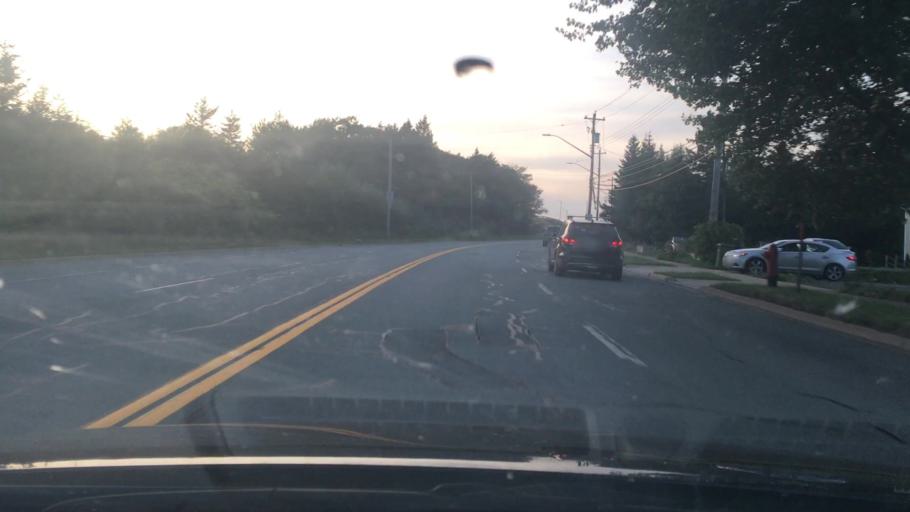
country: CA
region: Nova Scotia
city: Halifax
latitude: 44.6370
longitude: -63.5285
